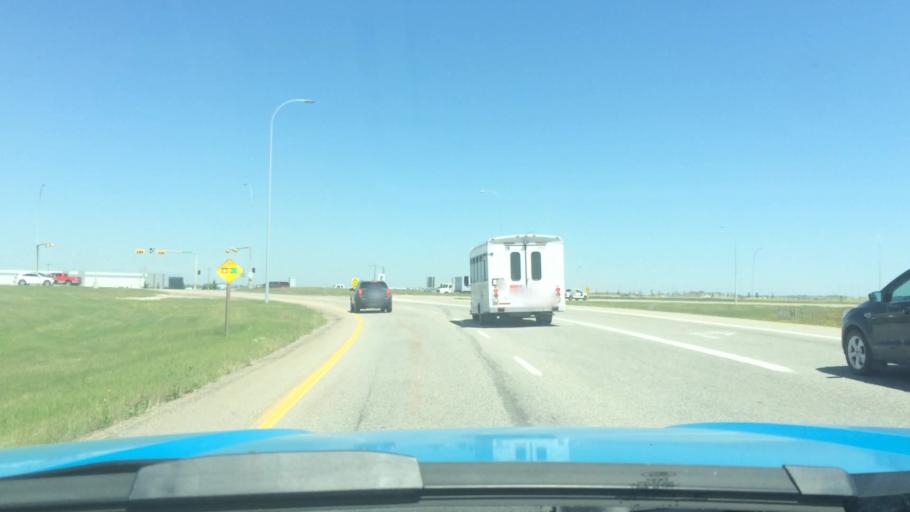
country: CA
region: Alberta
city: Calgary
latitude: 51.1532
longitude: -114.0155
